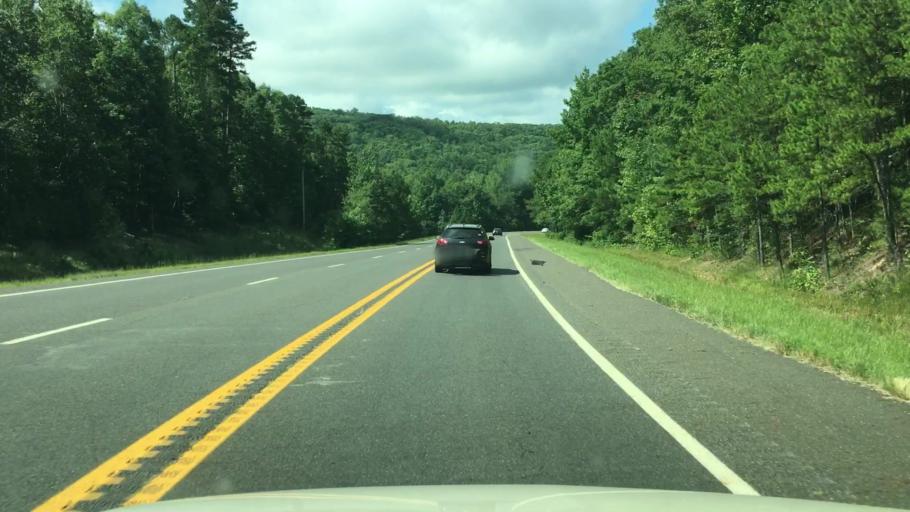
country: US
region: Arkansas
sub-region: Garland County
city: Lake Hamilton
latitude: 34.3645
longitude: -93.1622
